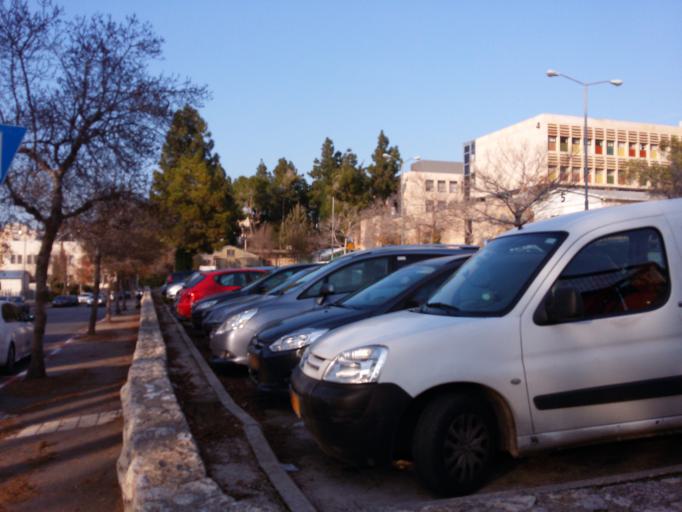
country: IL
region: Jerusalem
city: Jerusalem
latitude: 31.7771
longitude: 35.1955
